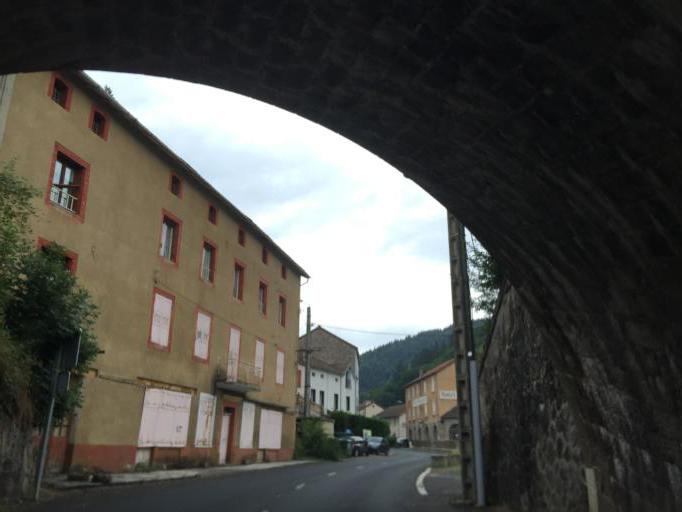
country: FR
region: Languedoc-Roussillon
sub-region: Departement de la Lozere
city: Langogne
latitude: 44.8379
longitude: 3.7381
